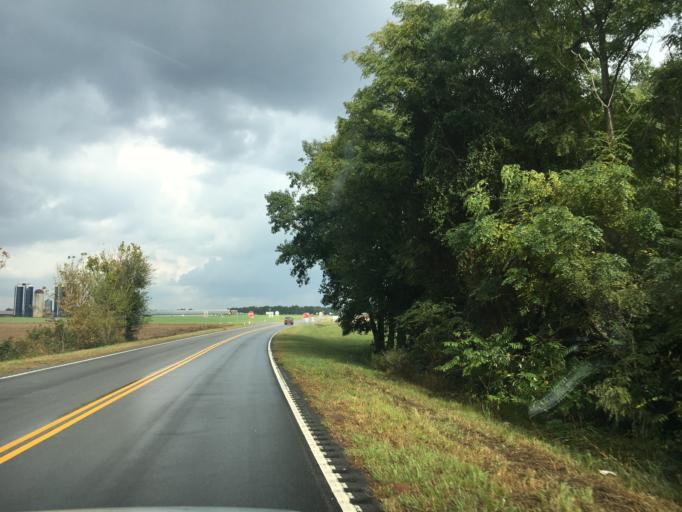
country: US
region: Georgia
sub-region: Hart County
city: Reed Creek
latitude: 34.4062
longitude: -82.7982
